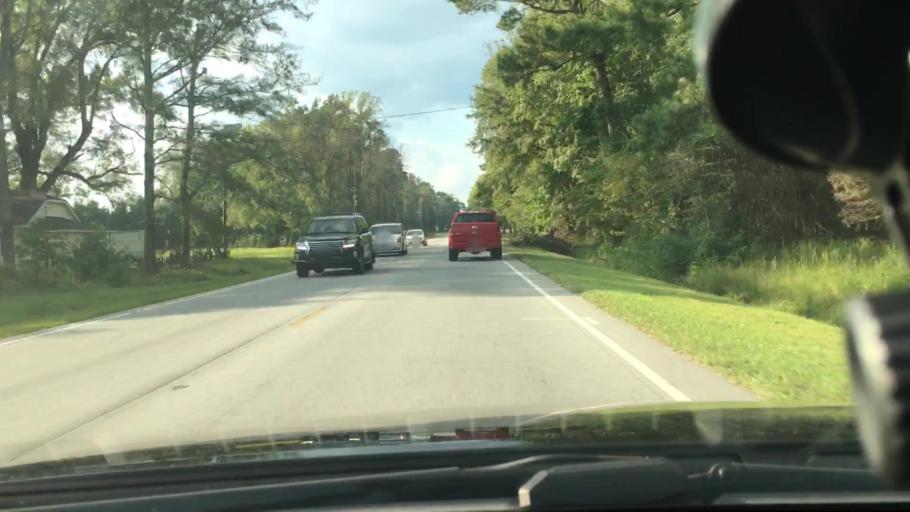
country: US
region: North Carolina
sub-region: Craven County
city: Vanceboro
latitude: 35.2594
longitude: -77.0994
